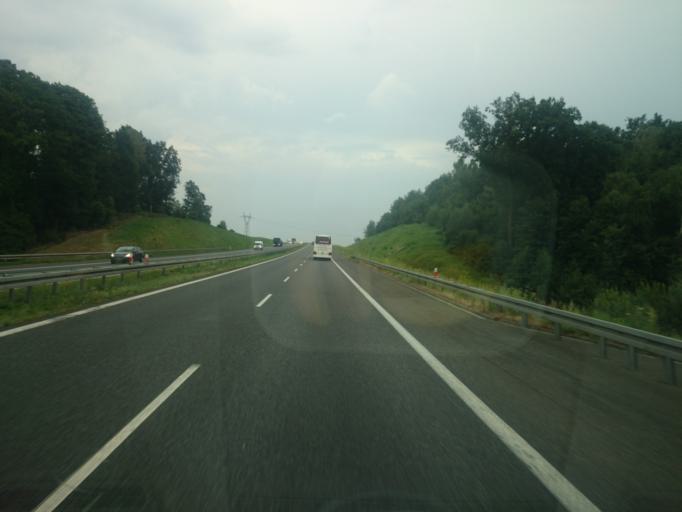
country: PL
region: Silesian Voivodeship
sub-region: Powiat gliwicki
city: Rudziniec
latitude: 50.4069
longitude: 18.4164
